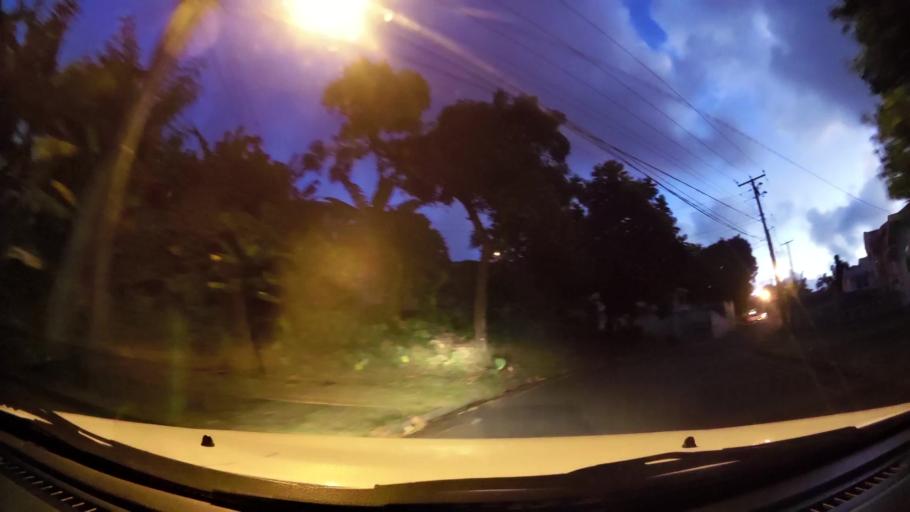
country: LC
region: Castries Quarter
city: Bisee
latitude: 14.0292
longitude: -60.9455
